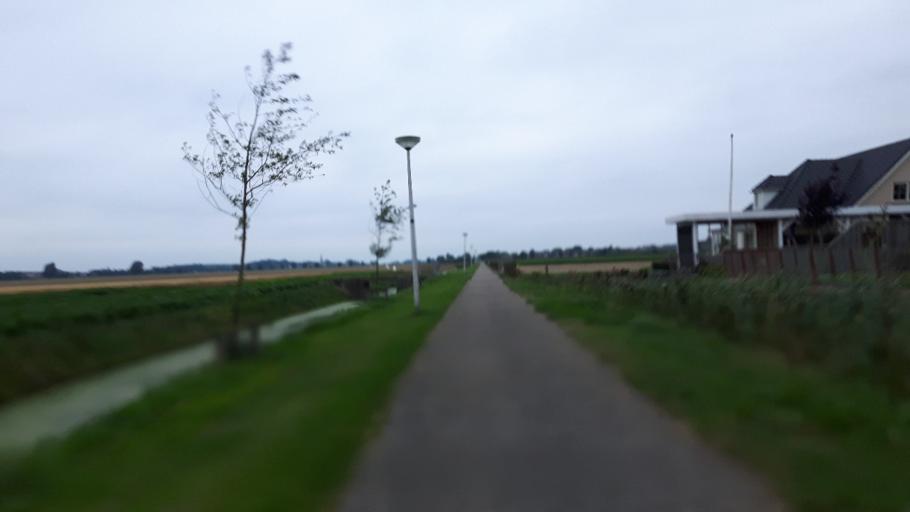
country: NL
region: South Holland
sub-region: Gemeente Nieuwkoop
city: Nieuwkoop
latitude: 52.1849
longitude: 4.7750
